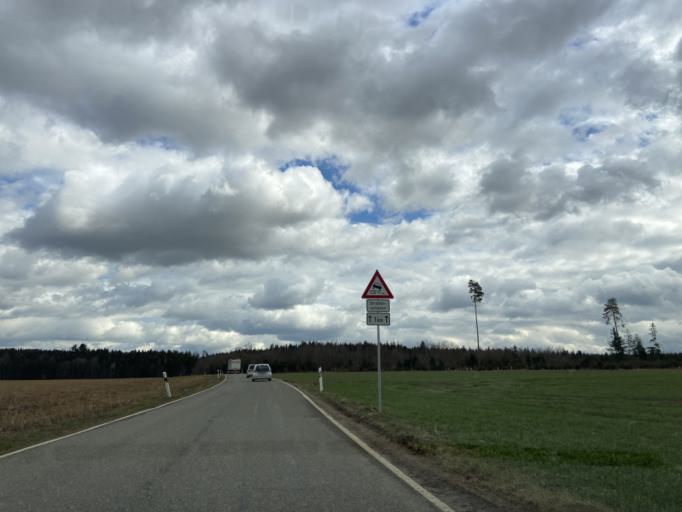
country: DE
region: Baden-Wuerttemberg
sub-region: Tuebingen Region
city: Ostrach
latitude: 47.9604
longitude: 9.3331
